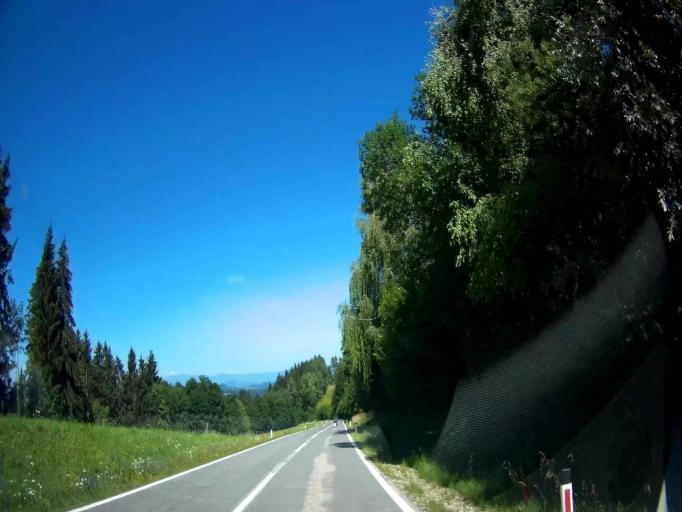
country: AT
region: Carinthia
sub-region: Politischer Bezirk Volkermarkt
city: Gallizien
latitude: 46.5533
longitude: 14.4755
